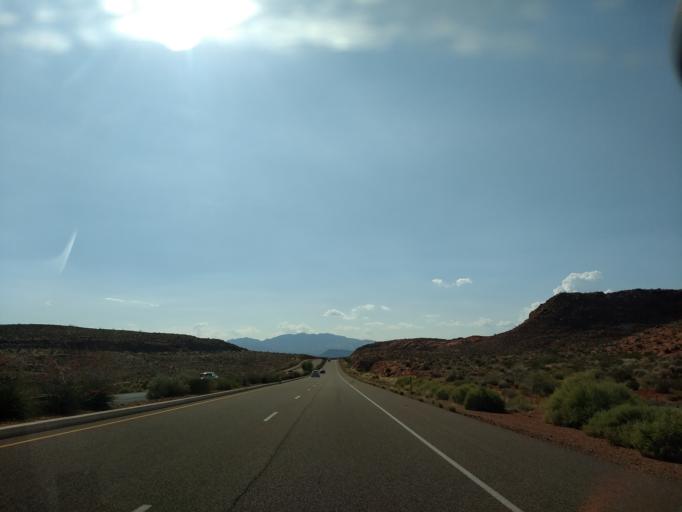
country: US
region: Utah
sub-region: Washington County
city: Saint George
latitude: 37.1339
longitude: -113.5904
